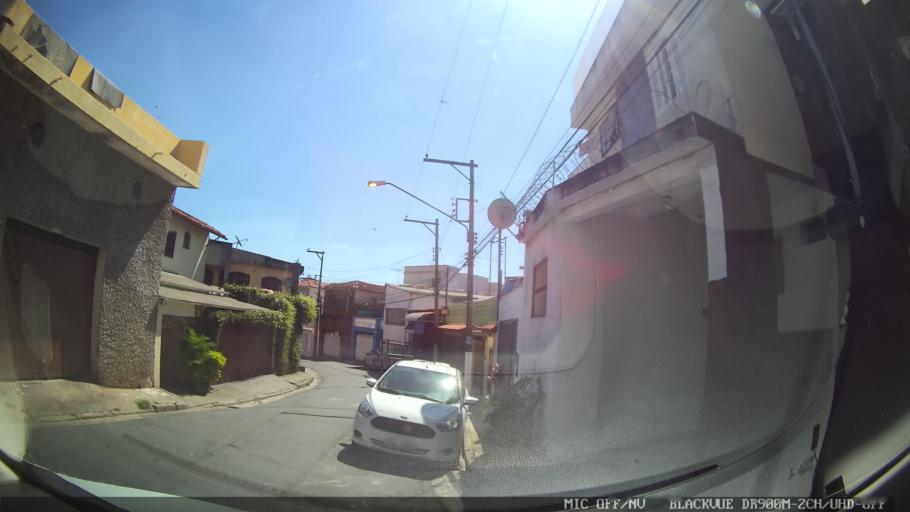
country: BR
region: Sao Paulo
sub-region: Sao Paulo
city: Sao Paulo
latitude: -23.4902
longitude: -46.6448
